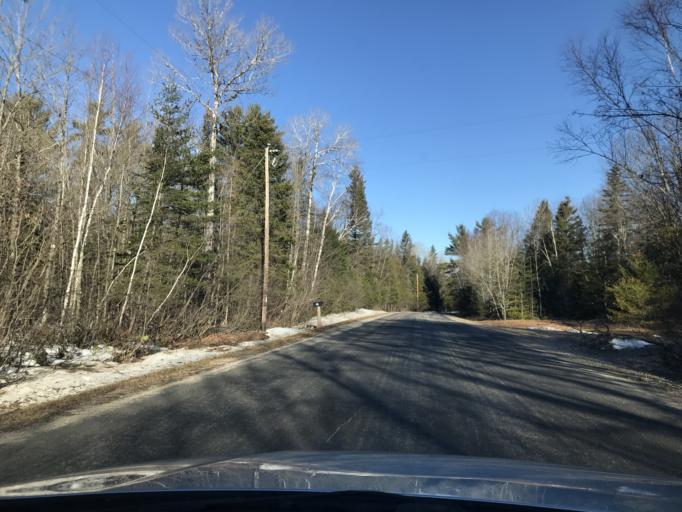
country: US
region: Wisconsin
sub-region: Marinette County
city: Niagara
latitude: 45.3750
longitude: -88.0198
